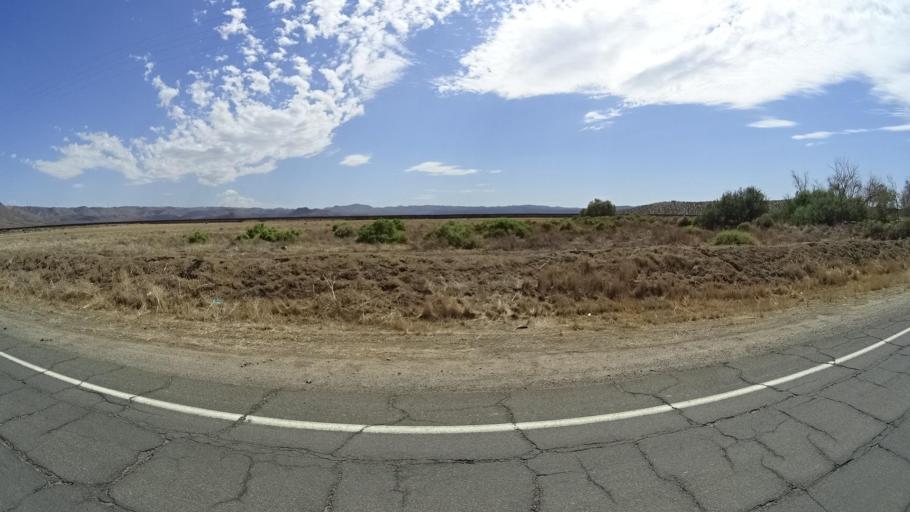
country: MX
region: Baja California
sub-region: Tecate
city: Cereso del Hongo
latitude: 32.6176
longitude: -116.1770
